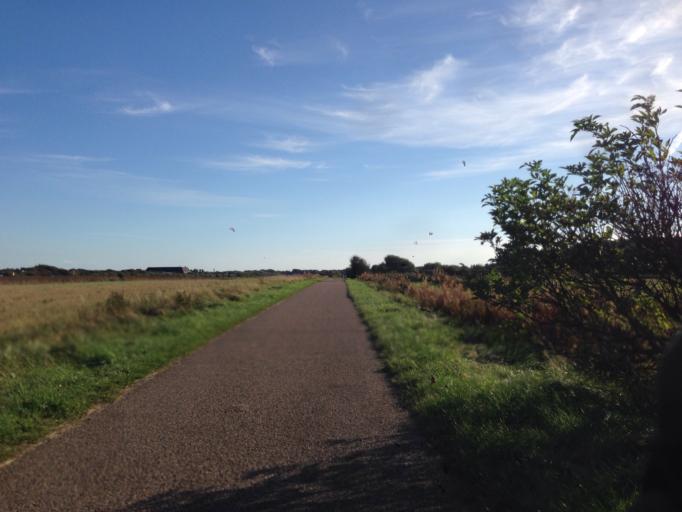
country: DE
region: Schleswig-Holstein
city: Tinnum
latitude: 54.9476
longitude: 8.3356
